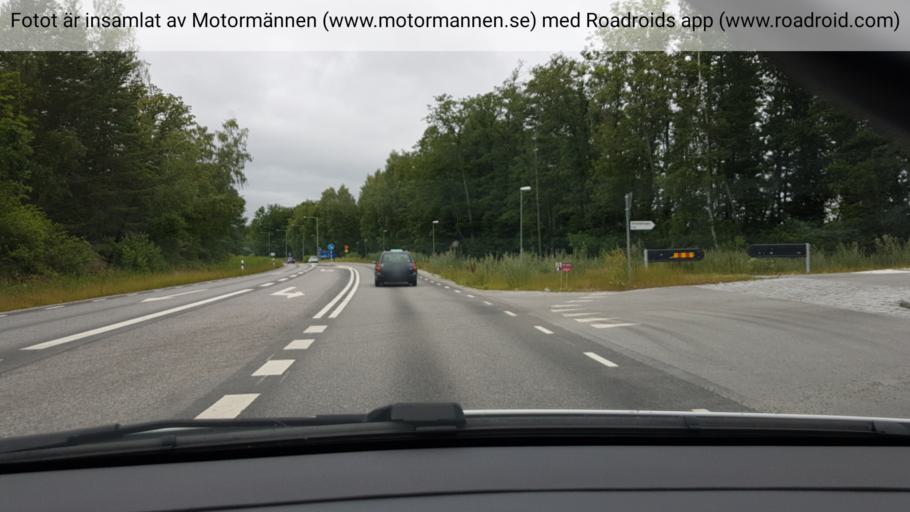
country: SE
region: Stockholm
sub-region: Vaxholms Kommun
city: Resaro
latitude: 59.4125
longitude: 18.3161
